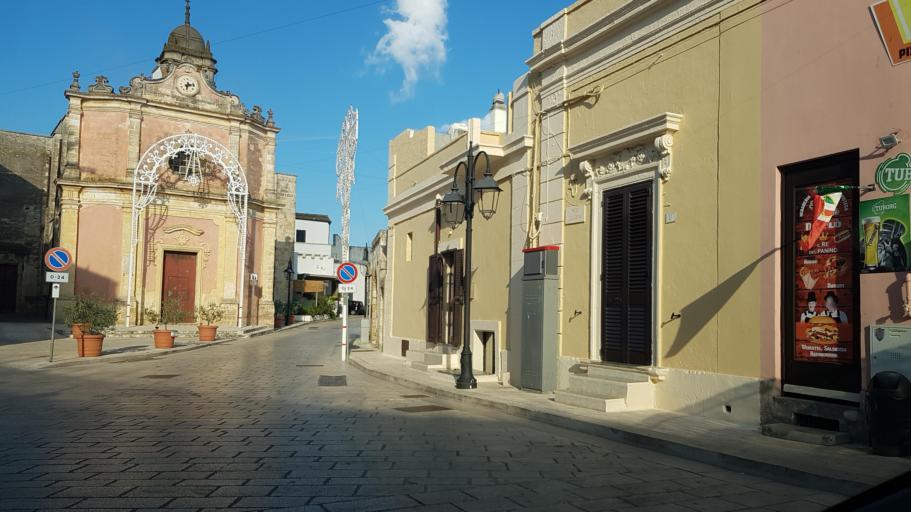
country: IT
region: Apulia
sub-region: Provincia di Lecce
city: Castiglione
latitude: 39.9824
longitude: 18.3481
